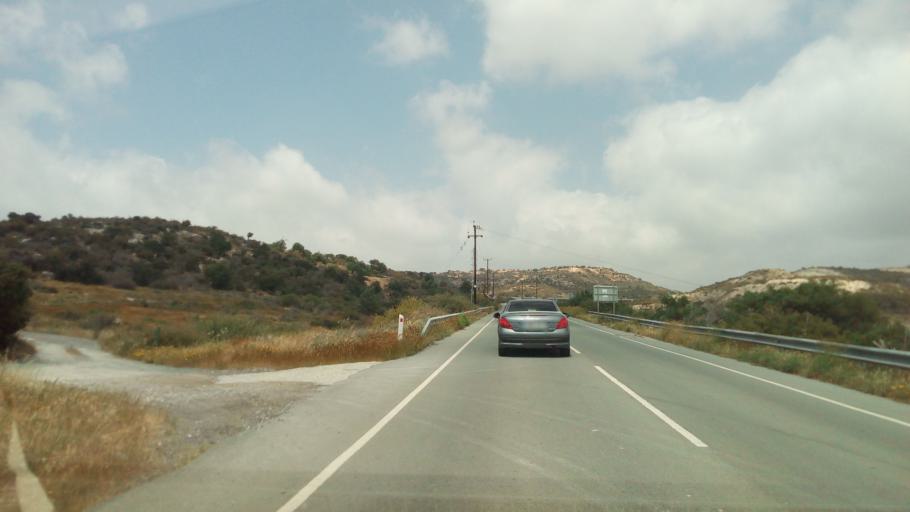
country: CY
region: Limassol
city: Pissouri
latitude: 34.6786
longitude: 32.7160
